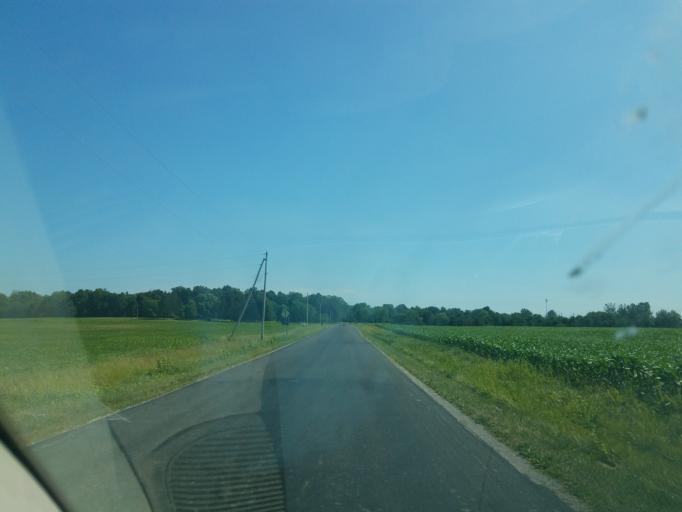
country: US
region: Ohio
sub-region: Crawford County
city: Bucyrus
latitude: 40.8111
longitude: -82.9355
